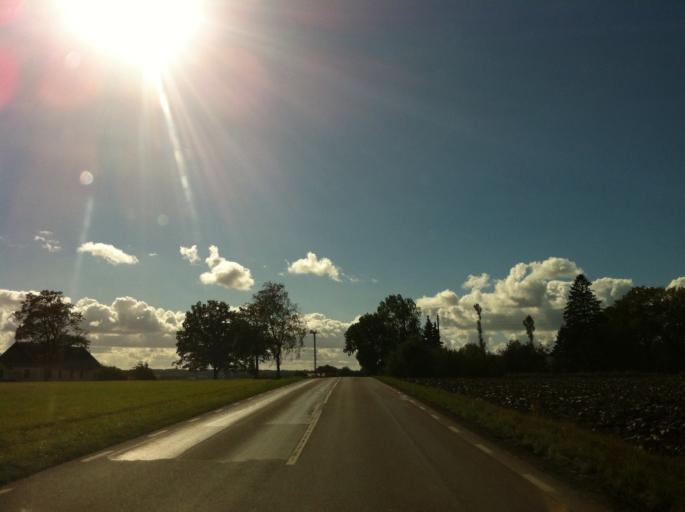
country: SE
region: Skane
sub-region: Sjobo Kommun
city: Sjoebo
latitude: 55.6487
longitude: 13.8049
